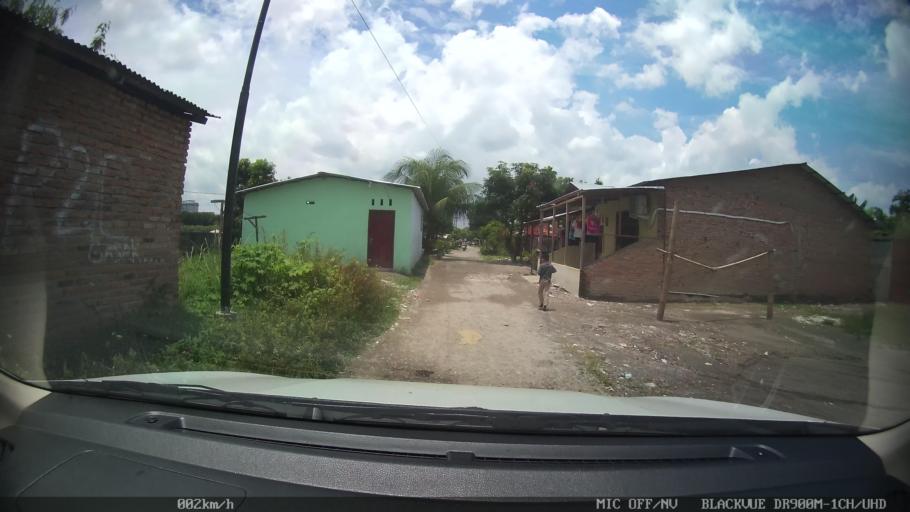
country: ID
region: North Sumatra
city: Medan
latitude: 3.6138
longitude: 98.7208
